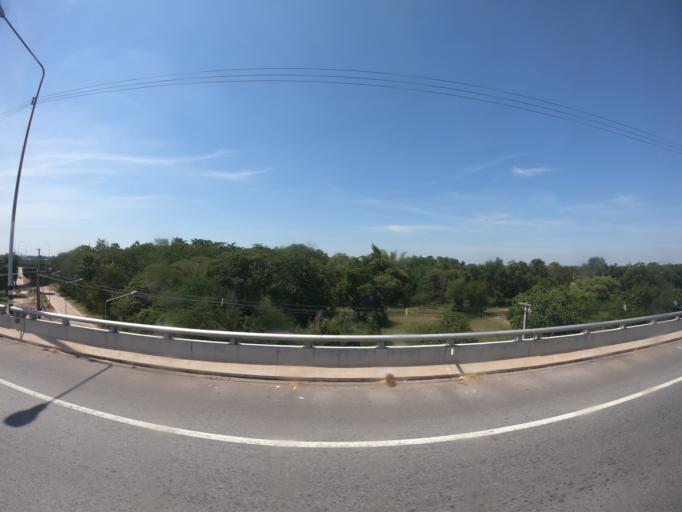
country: TH
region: Khon Kaen
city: Phon
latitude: 15.8300
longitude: 102.6077
